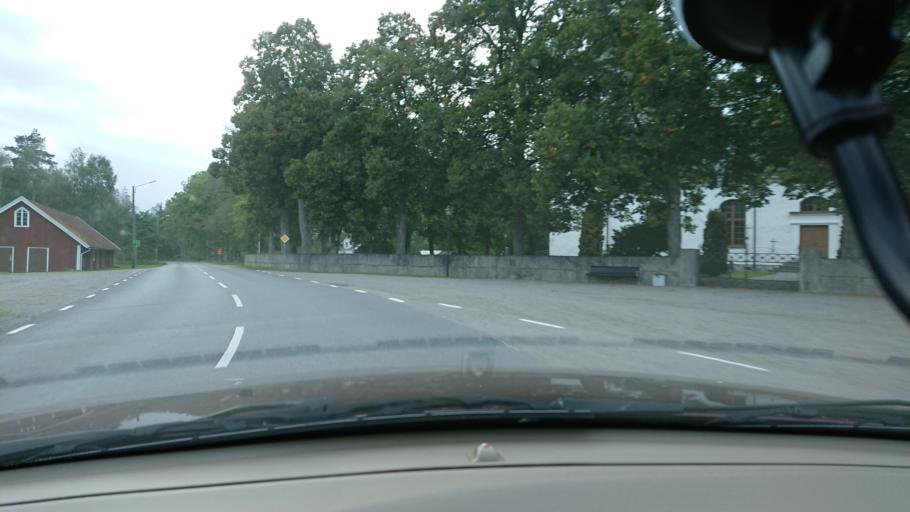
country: SE
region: Kronoberg
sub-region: Vaxjo Kommun
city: Lammhult
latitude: 57.0829
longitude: 14.7091
